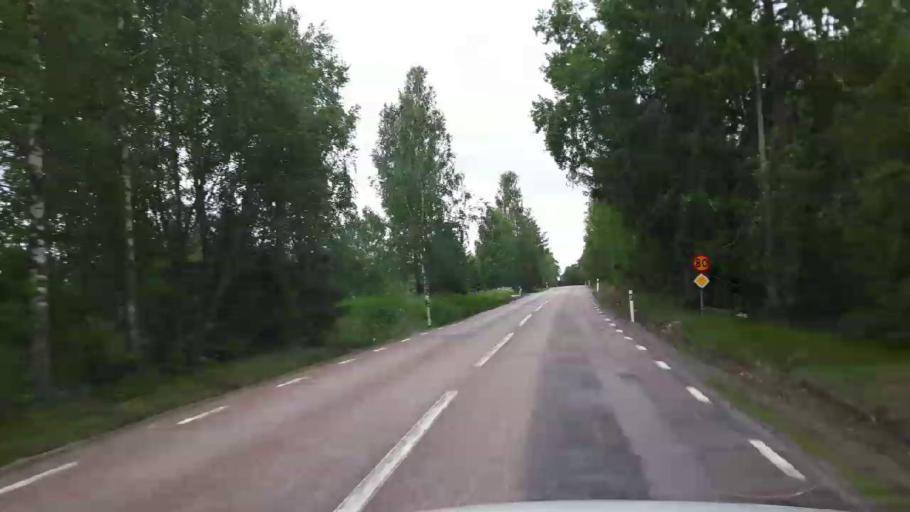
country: SE
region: Vaestmanland
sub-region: Kopings Kommun
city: Kolsva
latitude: 59.6979
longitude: 15.7829
